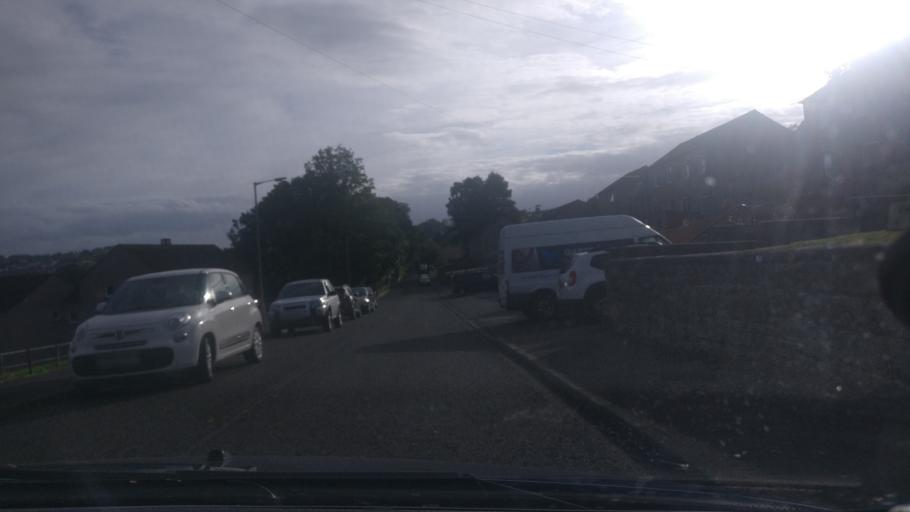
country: GB
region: Scotland
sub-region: The Scottish Borders
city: Hawick
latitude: 55.4331
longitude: -2.7845
